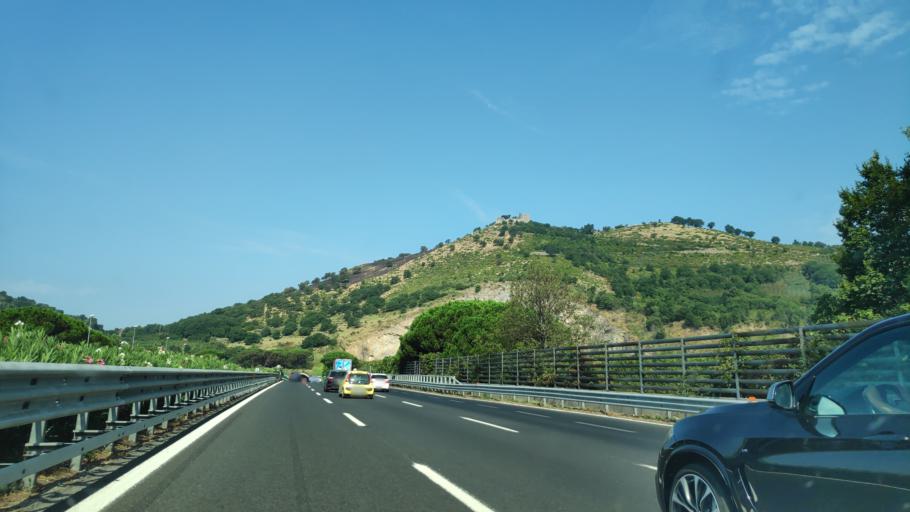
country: IT
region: Campania
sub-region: Provincia di Salerno
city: Lanzara
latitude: 40.7715
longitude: 14.6658
